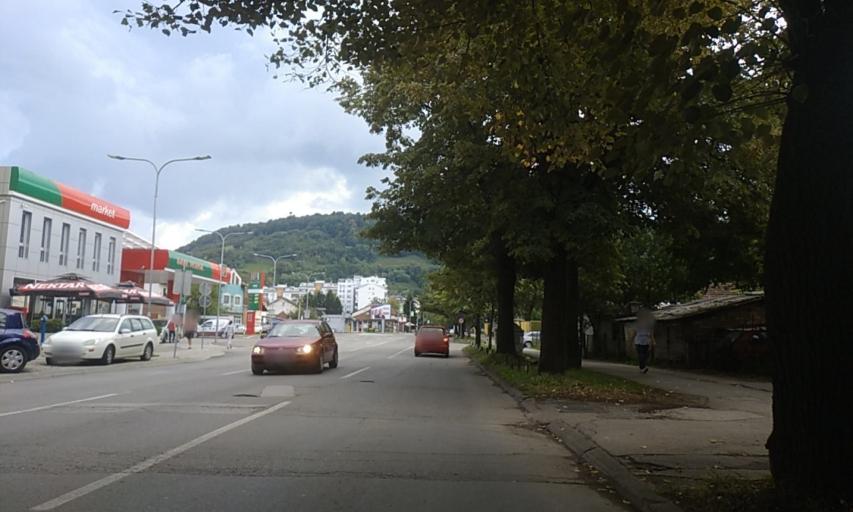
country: BA
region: Republika Srpska
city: Mejdan - Obilicevo
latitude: 44.7616
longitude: 17.1917
